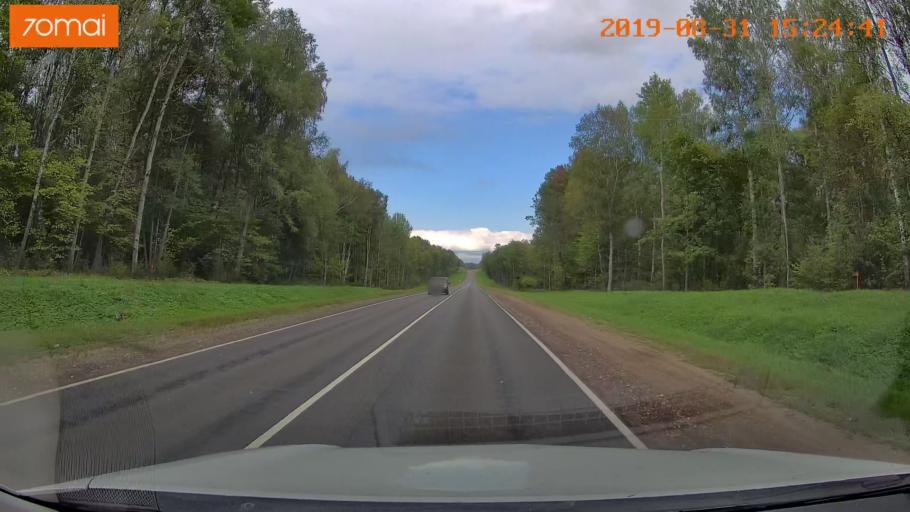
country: RU
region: Kaluga
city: Baryatino
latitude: 54.5312
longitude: 34.5085
